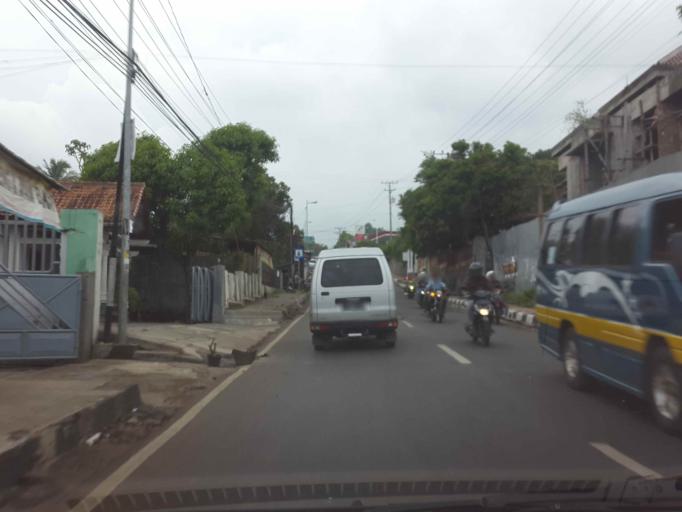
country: ID
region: Central Java
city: Salatiga
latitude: -7.3189
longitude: 110.5046
